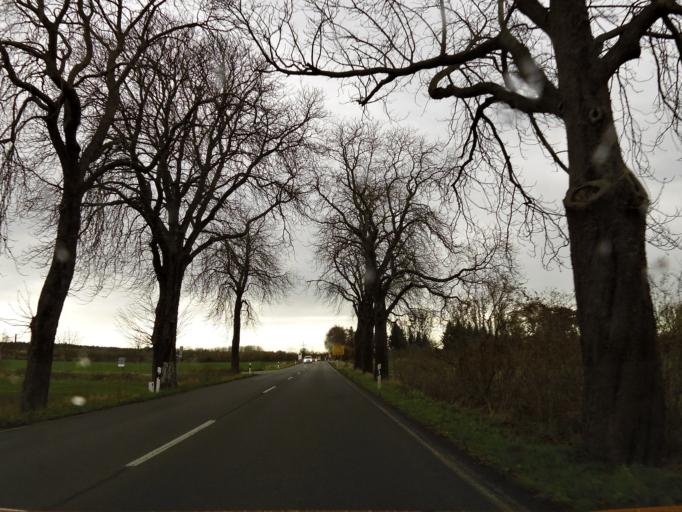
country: DE
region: Saxony-Anhalt
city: Gardelegen
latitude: 52.5306
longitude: 11.3768
